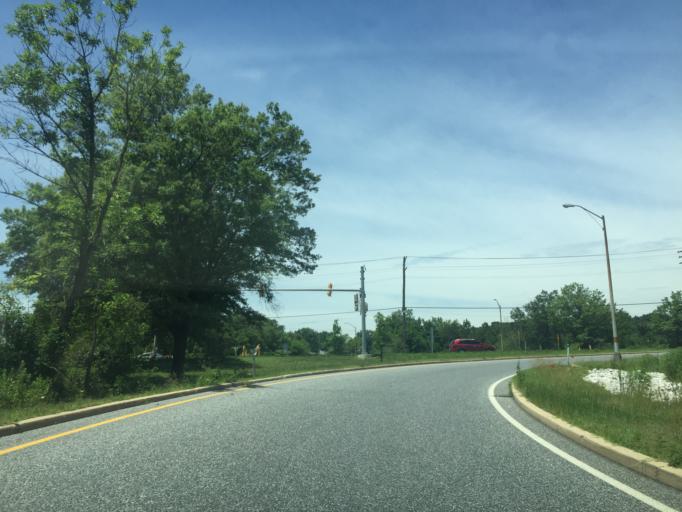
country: US
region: Maryland
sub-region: Baltimore County
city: Carney
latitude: 39.3870
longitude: -76.5305
